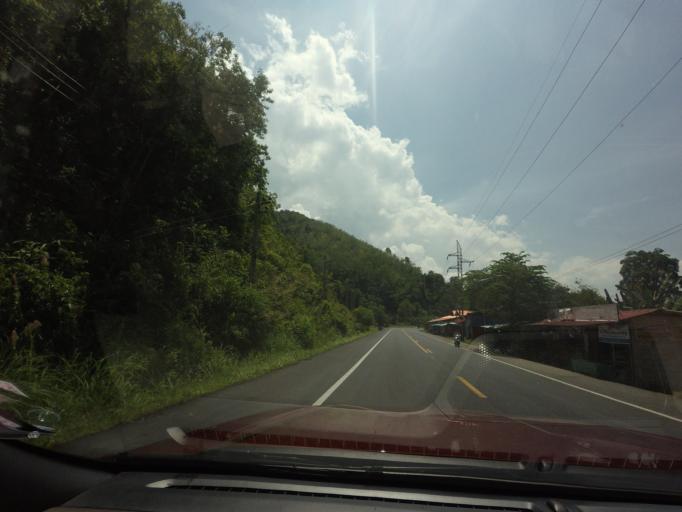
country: TH
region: Yala
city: Than To
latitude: 5.9712
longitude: 101.2004
